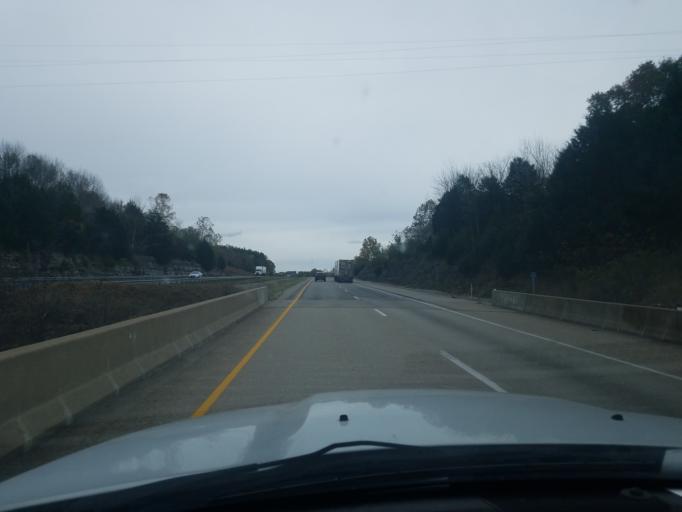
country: US
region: Indiana
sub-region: Harrison County
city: Corydon
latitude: 38.2361
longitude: -86.2266
